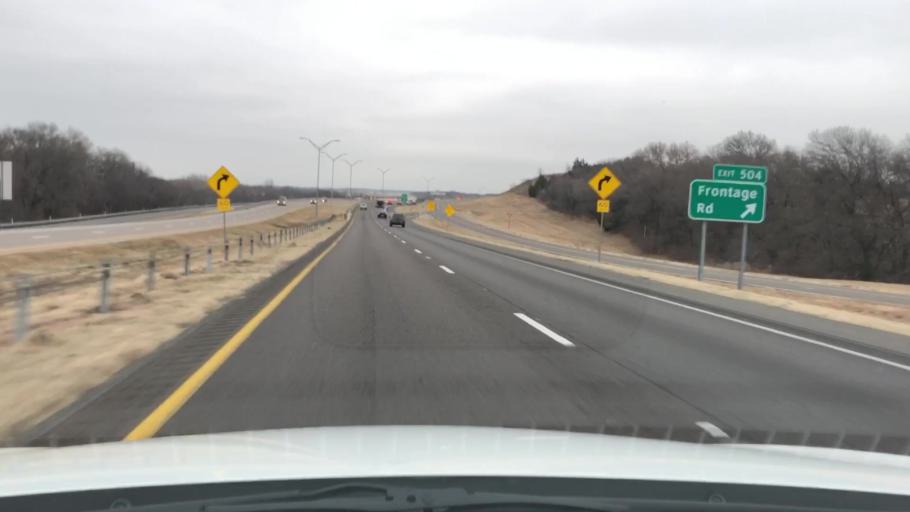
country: US
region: Texas
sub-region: Cooke County
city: Gainesville
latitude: 33.7212
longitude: -97.1611
